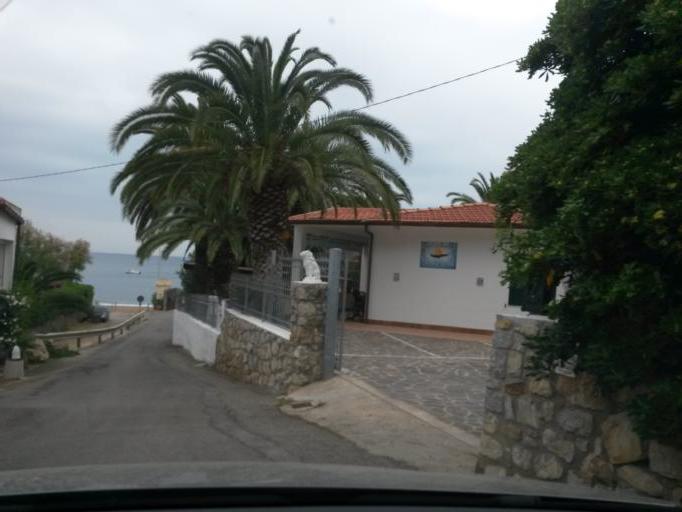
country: IT
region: Tuscany
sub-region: Provincia di Livorno
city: Capoliveri
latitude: 42.7280
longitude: 10.3765
